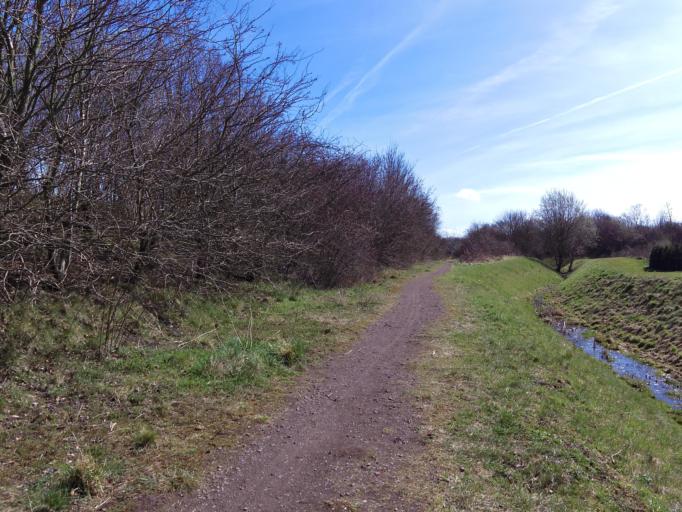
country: DE
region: Saxony
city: Borsdorf
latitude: 51.3371
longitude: 12.4973
